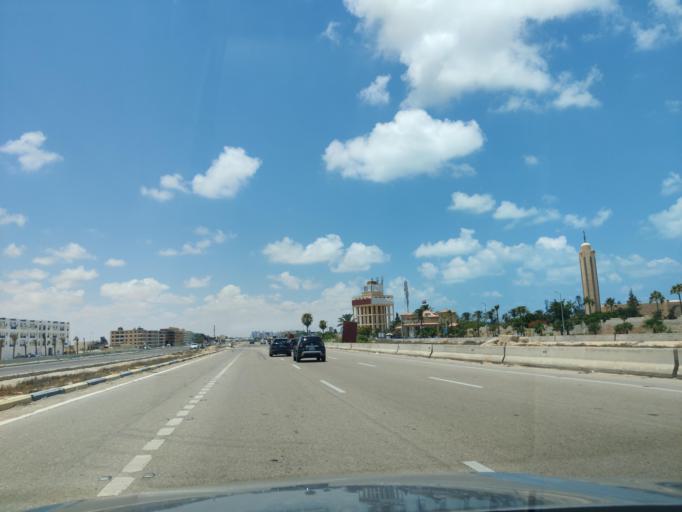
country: EG
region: Muhafazat Matruh
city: Al `Alamayn
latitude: 30.8166
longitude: 29.0331
